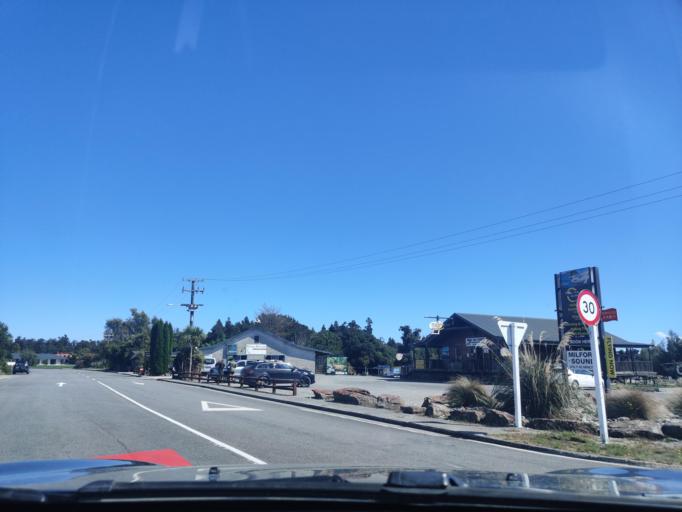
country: NZ
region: Otago
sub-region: Queenstown-Lakes District
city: Wanaka
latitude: -43.8792
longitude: 169.0436
